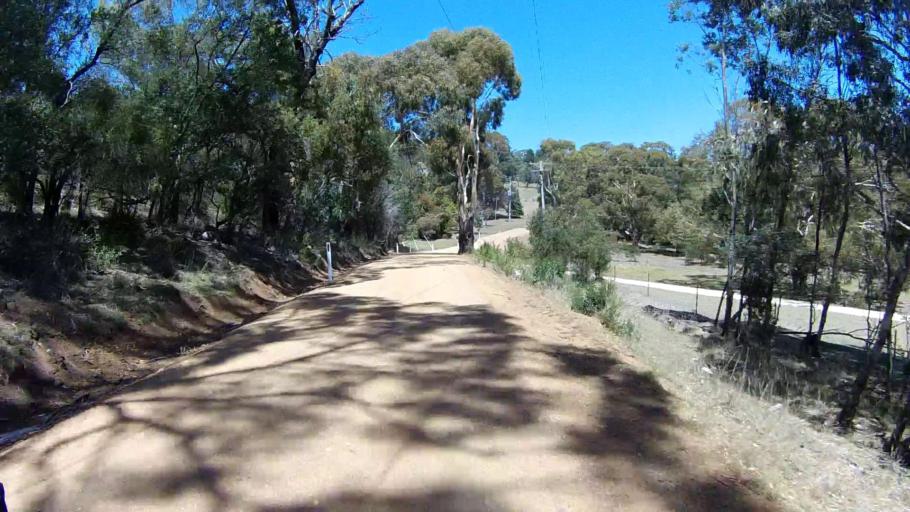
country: AU
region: Tasmania
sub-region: Clarence
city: Cambridge
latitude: -42.8508
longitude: 147.4381
